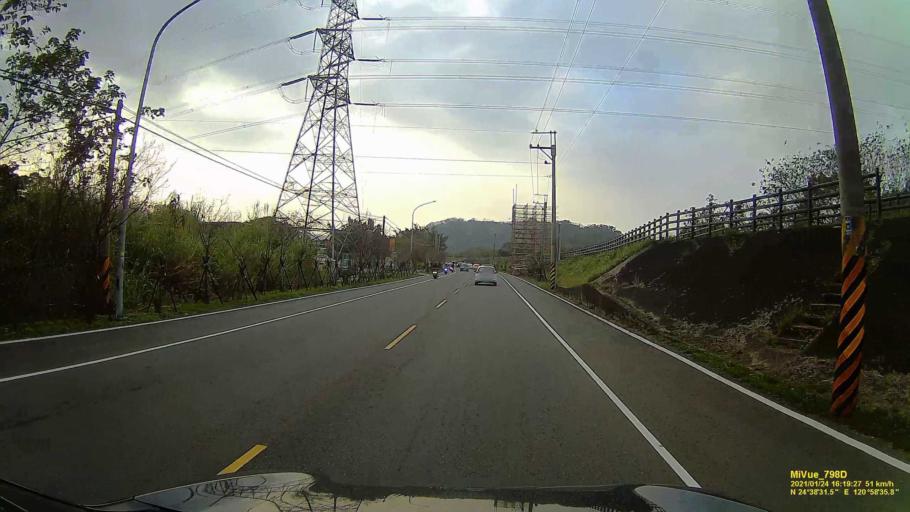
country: TW
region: Taiwan
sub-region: Hsinchu
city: Hsinchu
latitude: 24.6421
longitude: 120.9764
